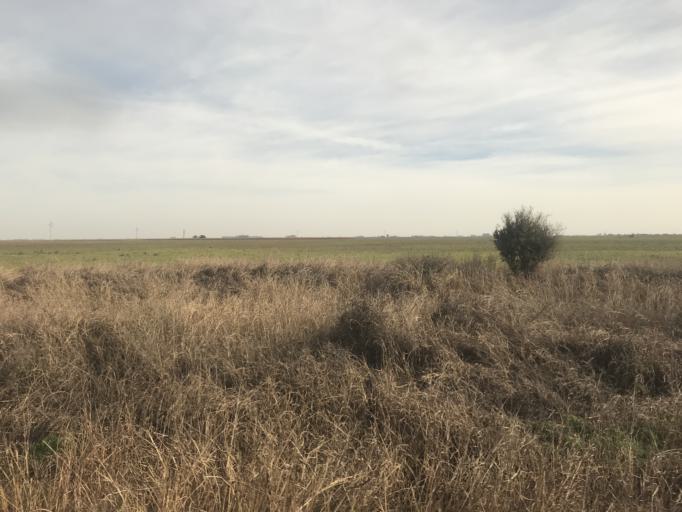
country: AR
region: Cordoba
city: Pilar
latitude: -31.6970
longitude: -63.8728
